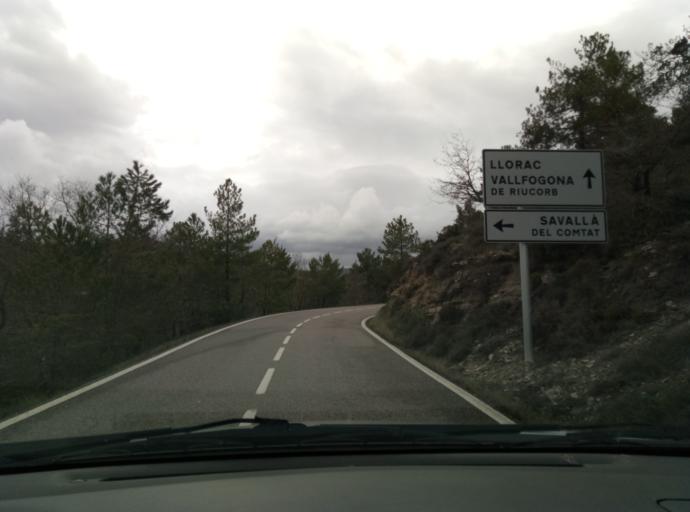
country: ES
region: Catalonia
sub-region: Provincia de Tarragona
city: Conesa
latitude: 41.5439
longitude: 1.3266
